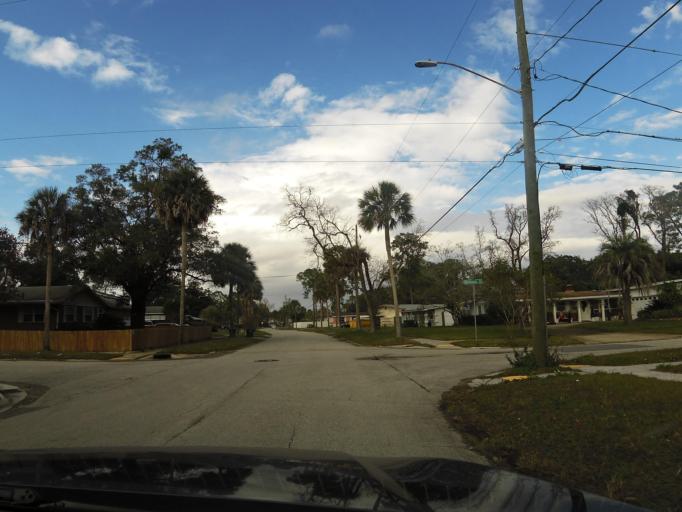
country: US
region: Florida
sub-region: Duval County
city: Jacksonville
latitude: 30.3394
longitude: -81.5653
